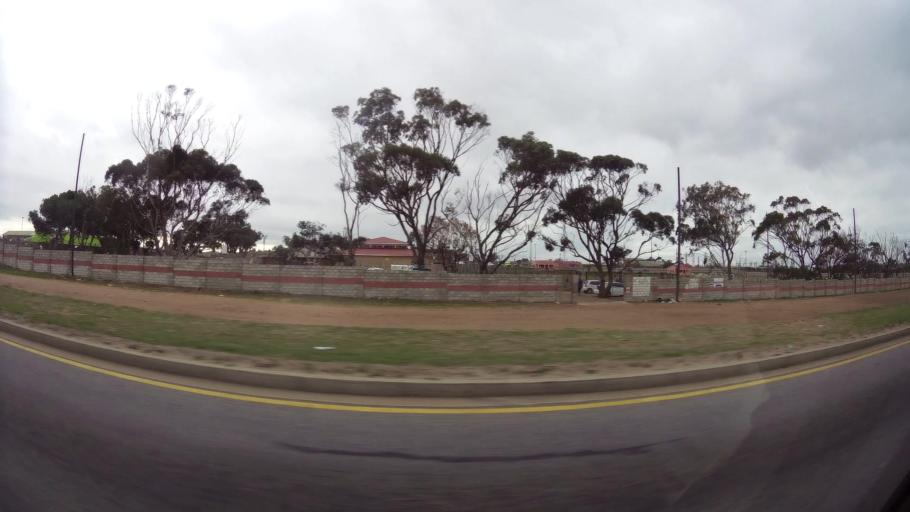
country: ZA
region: Eastern Cape
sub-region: Nelson Mandela Bay Metropolitan Municipality
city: Port Elizabeth
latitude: -33.9119
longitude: 25.5596
